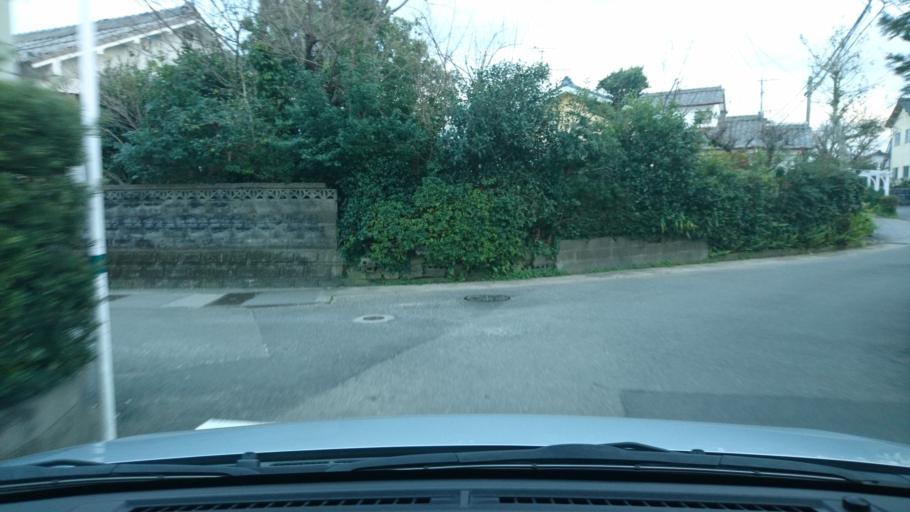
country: JP
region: Miyazaki
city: Miyazaki-shi
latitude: 31.8550
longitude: 131.4313
